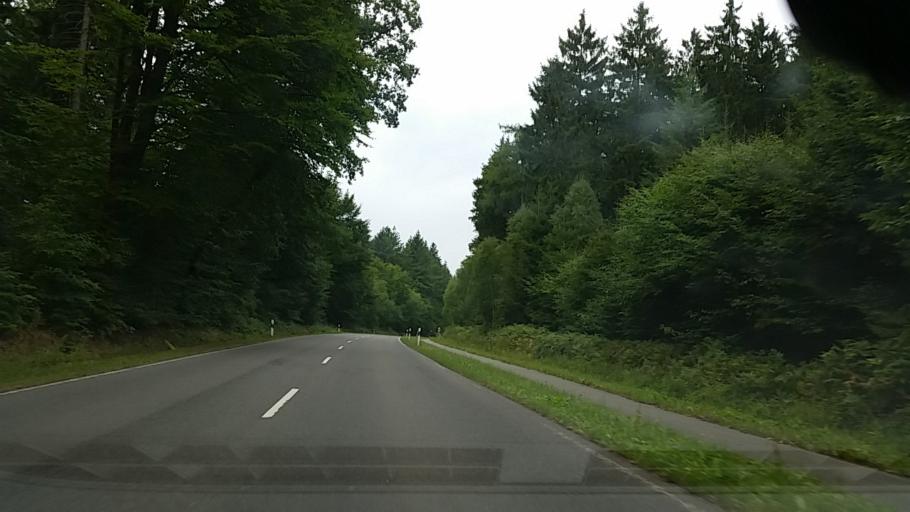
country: DE
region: Schleswig-Holstein
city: Aumuhle
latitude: 53.5192
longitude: 10.3460
